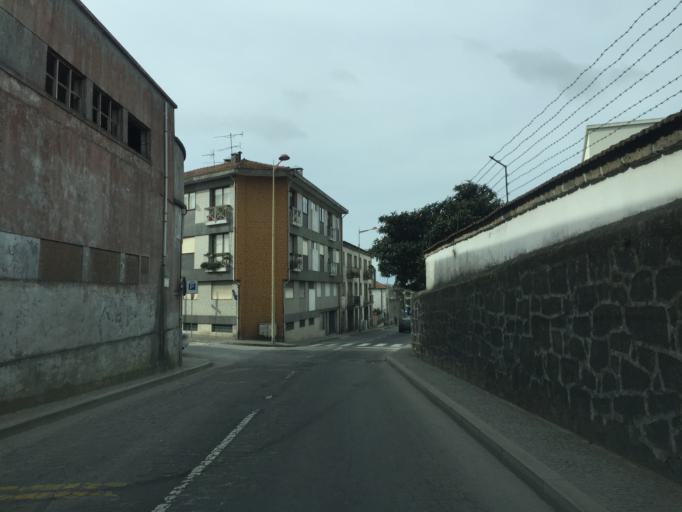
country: PT
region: Porto
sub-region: Porto
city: Porto
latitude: 41.1378
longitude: -8.6046
